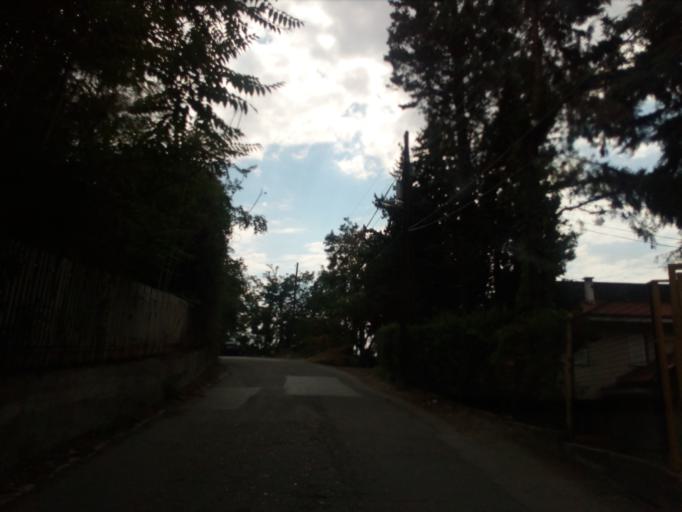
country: MK
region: Veles
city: Veles
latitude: 41.7166
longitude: 21.7761
